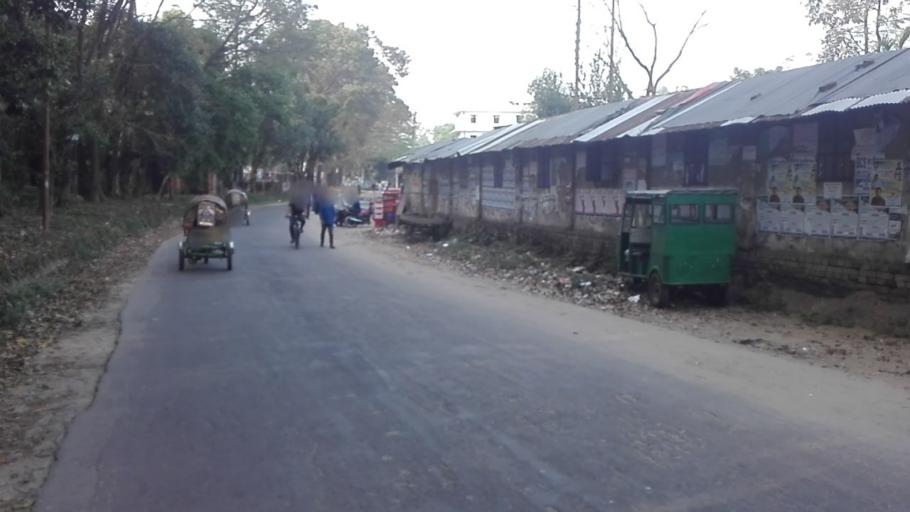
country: BD
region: Chittagong
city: Chittagong
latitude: 22.4716
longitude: 91.7933
